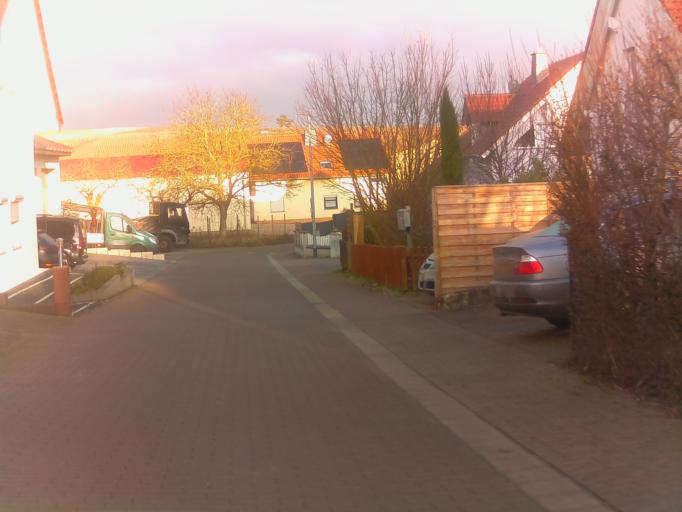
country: DE
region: Rheinland-Pfalz
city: Wendelsheim
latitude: 49.7609
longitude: 7.9848
